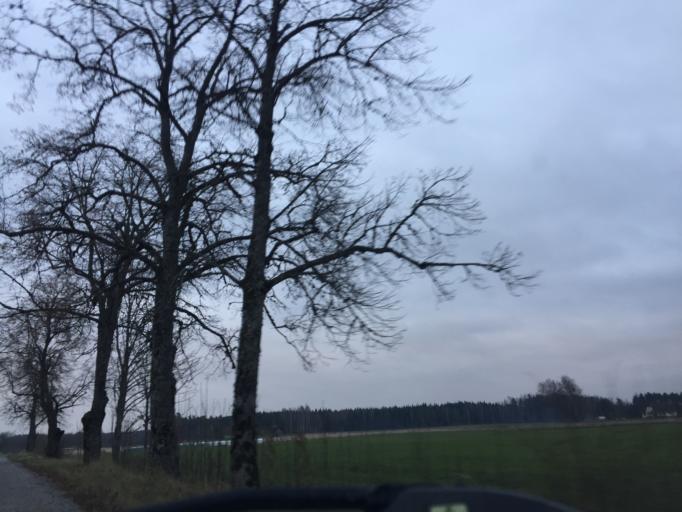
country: LV
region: Aloja
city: Aloja
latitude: 57.6911
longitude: 24.8883
